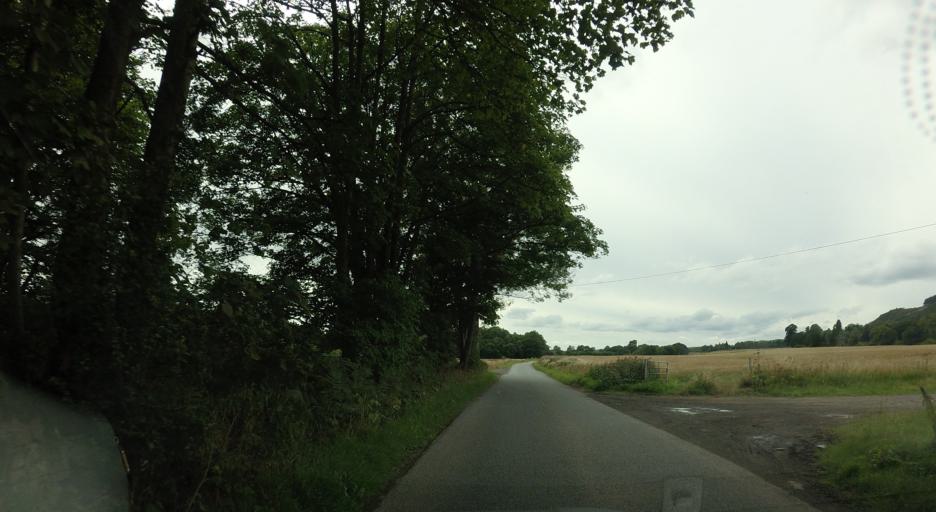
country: GB
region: Scotland
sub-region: Perth and Kinross
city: Bridge of Earn
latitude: 56.3540
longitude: -3.3893
